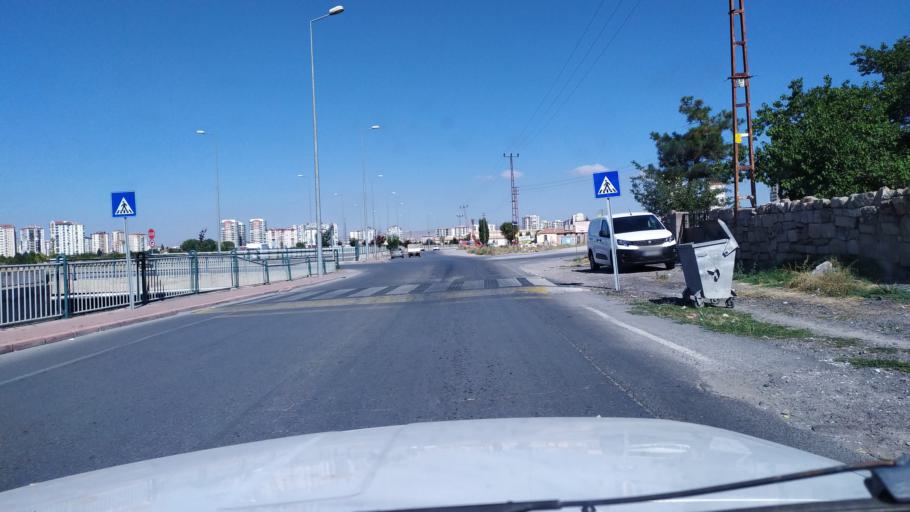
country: TR
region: Kayseri
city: Talas
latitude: 38.7338
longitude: 35.5481
